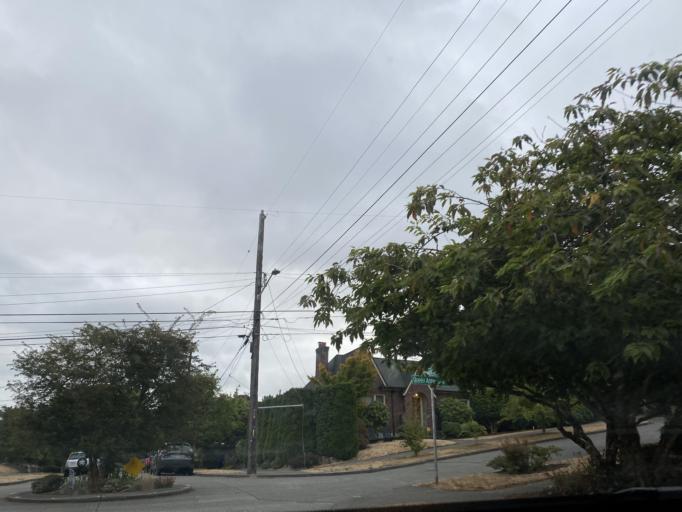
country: US
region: Washington
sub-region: King County
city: Seattle
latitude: 47.6441
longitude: -122.3573
